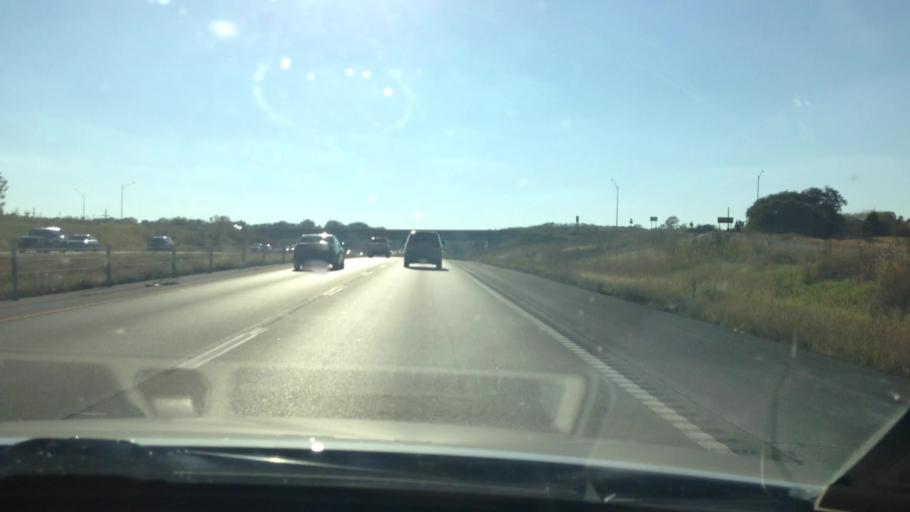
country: US
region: Missouri
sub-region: Clay County
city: Gladstone
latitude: 39.2579
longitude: -94.5978
